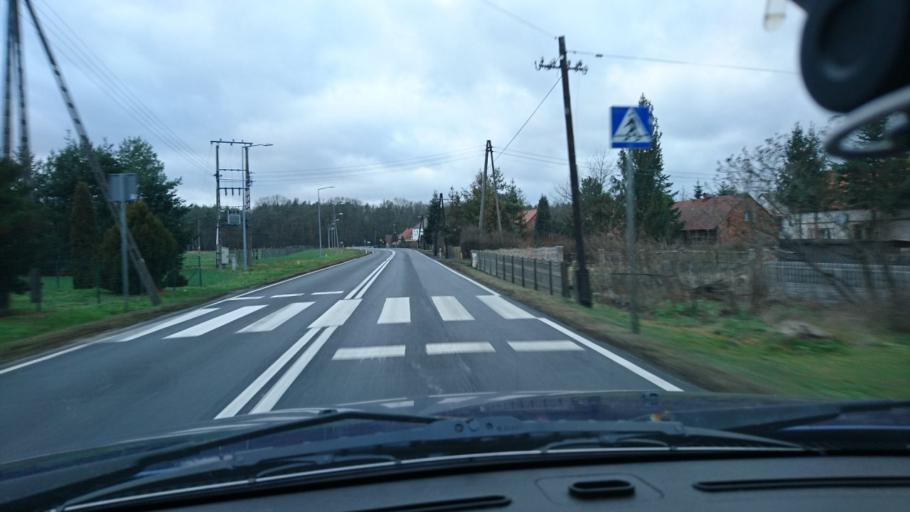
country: PL
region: Opole Voivodeship
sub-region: Powiat kluczborski
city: Kluczbork
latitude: 50.9462
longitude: 18.3187
